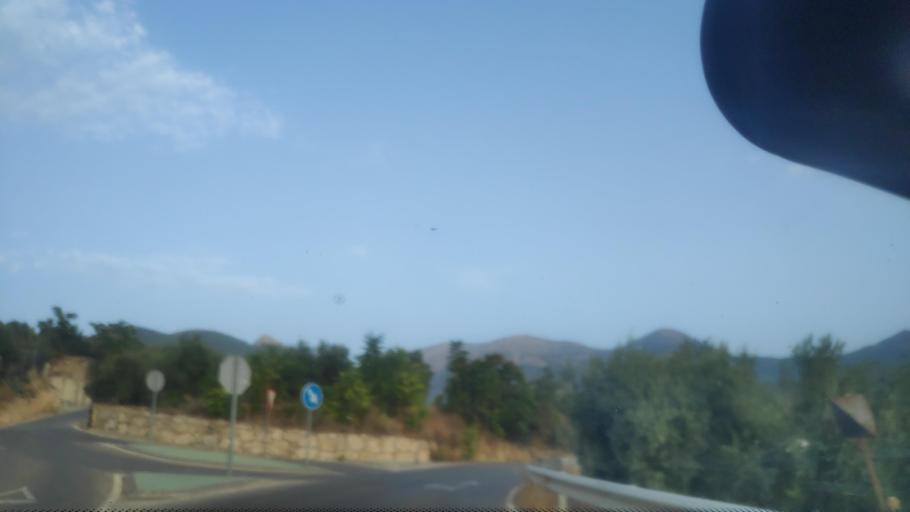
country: ES
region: Andalusia
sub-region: Provincia de Jaen
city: Torres
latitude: 37.7895
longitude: -3.5170
